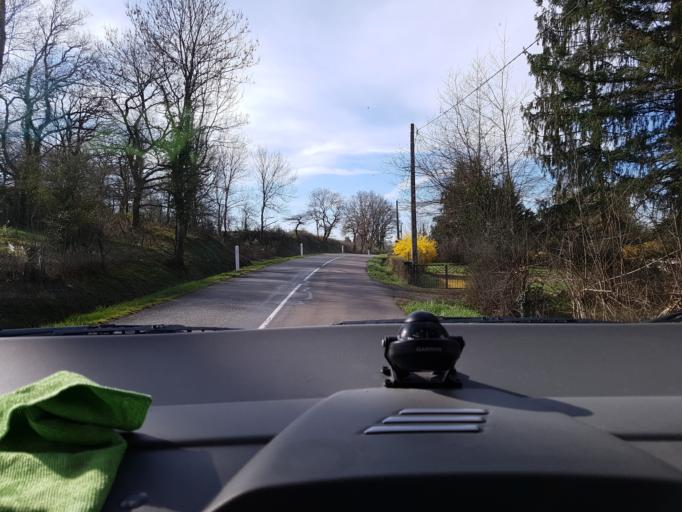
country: FR
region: Bourgogne
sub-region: Departement de Saone-et-Loire
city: Toulon-sur-Arroux
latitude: 46.7149
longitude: 4.1359
